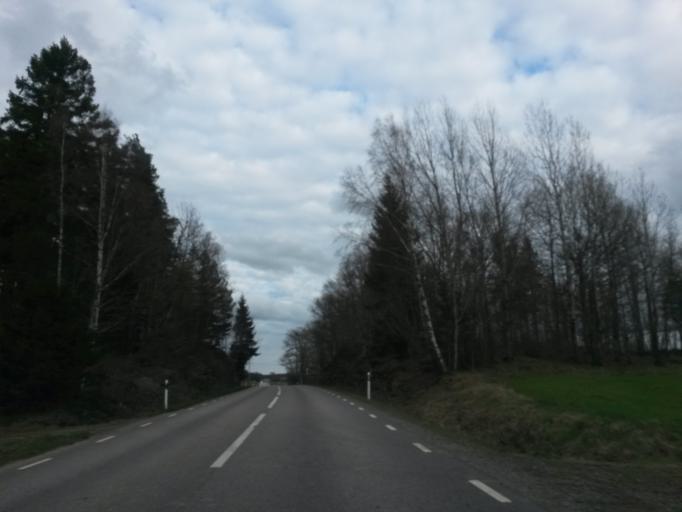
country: SE
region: Vaestra Goetaland
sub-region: Vargarda Kommun
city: Vargarda
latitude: 58.0547
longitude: 12.7613
